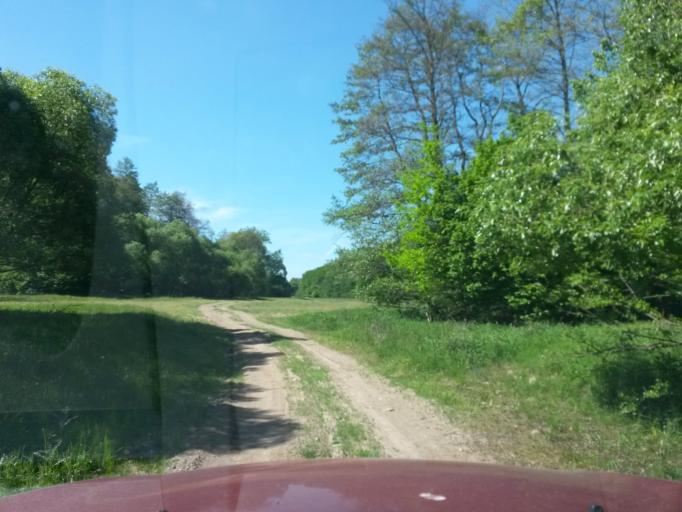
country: SK
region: Presovsky
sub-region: Okres Presov
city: Presov
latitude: 48.8860
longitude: 21.3949
